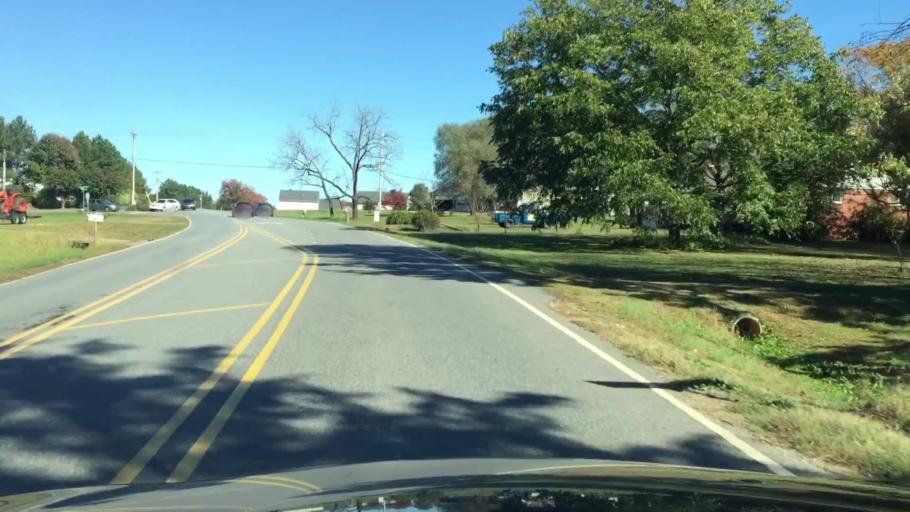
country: US
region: North Carolina
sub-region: Iredell County
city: Mooresville
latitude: 35.5404
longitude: -80.7892
